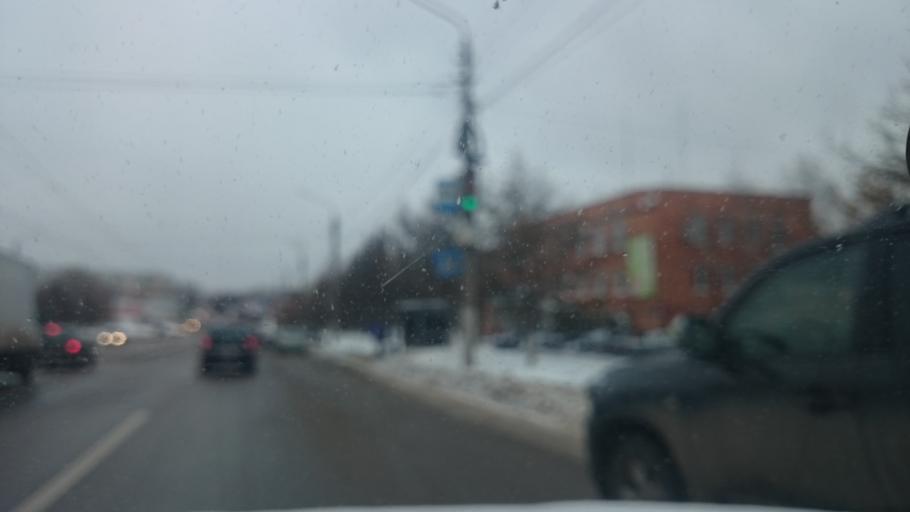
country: RU
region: Tula
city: Tula
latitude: 54.2017
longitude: 37.6272
